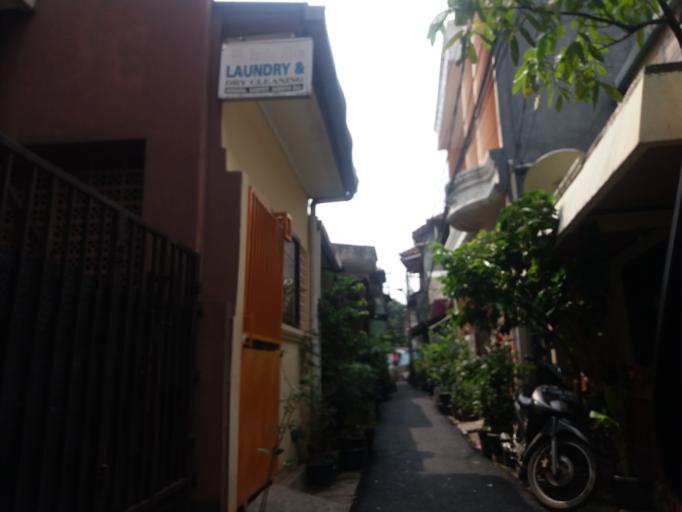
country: ID
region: Jakarta Raya
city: Jakarta
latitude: -6.1901
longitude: 106.8196
